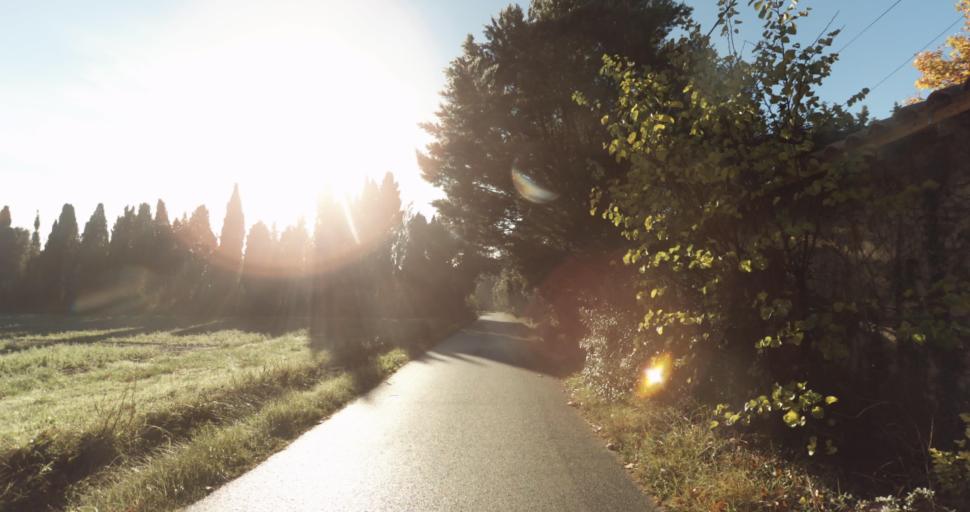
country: FR
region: Provence-Alpes-Cote d'Azur
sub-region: Departement des Bouches-du-Rhone
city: Rognonas
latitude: 43.8809
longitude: 4.7983
